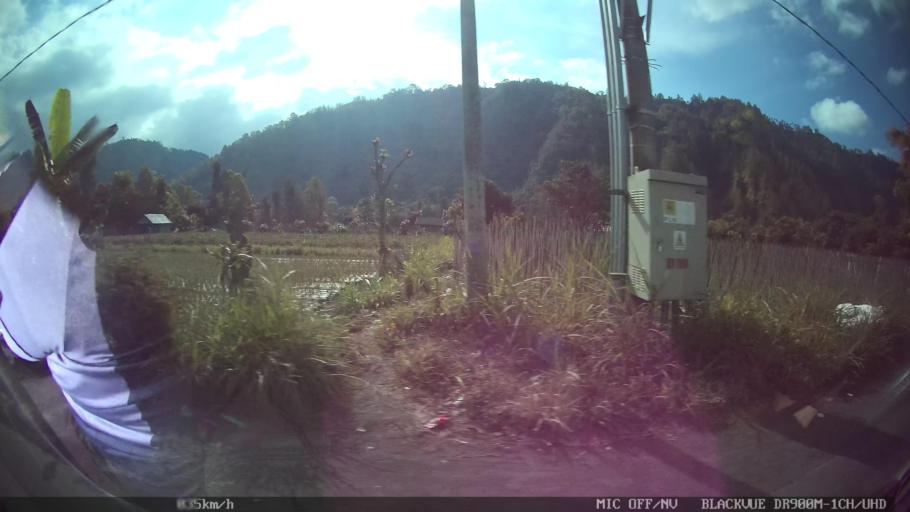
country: ID
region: Bali
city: Banjar Kedisan
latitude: -8.2237
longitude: 115.3609
